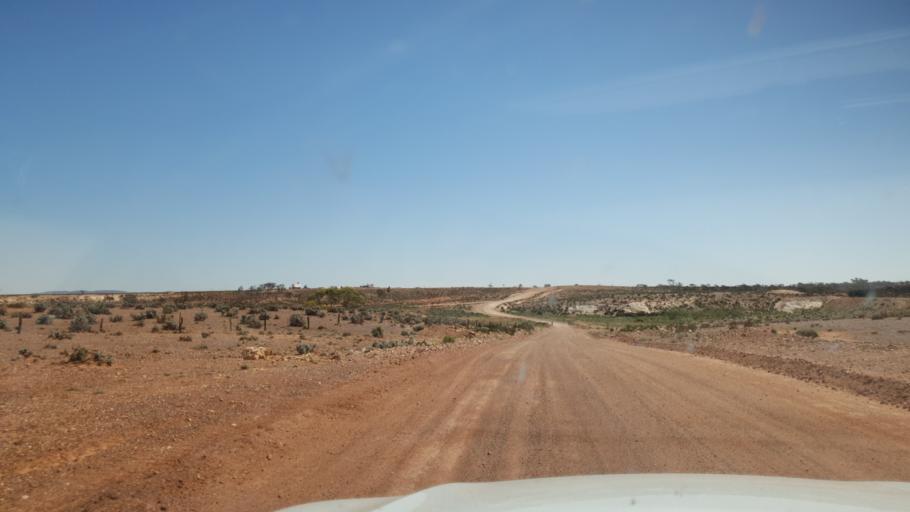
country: AU
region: South Australia
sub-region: Whyalla
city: Whyalla
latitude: -32.6487
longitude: 136.9667
